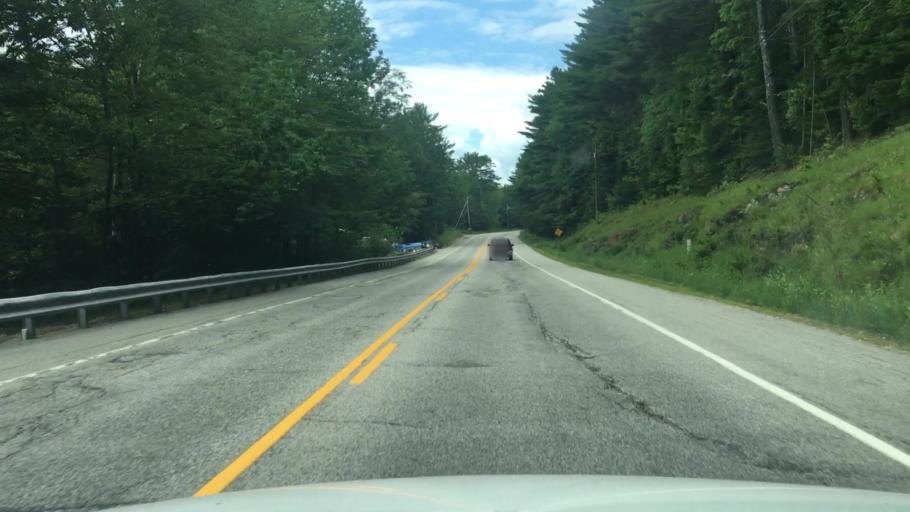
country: US
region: Maine
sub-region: Oxford County
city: West Paris
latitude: 44.3412
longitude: -70.5604
